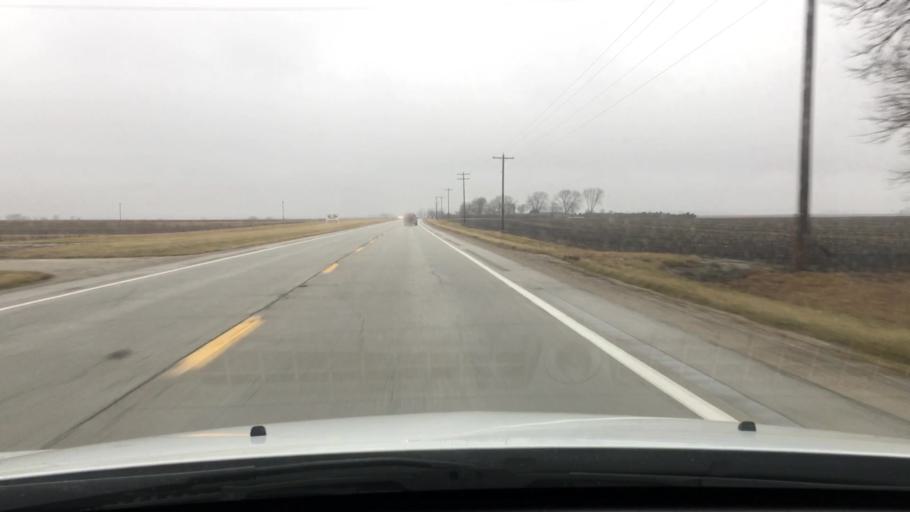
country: US
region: Illinois
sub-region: Livingston County
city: Flanagan
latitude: 40.8718
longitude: -88.8104
